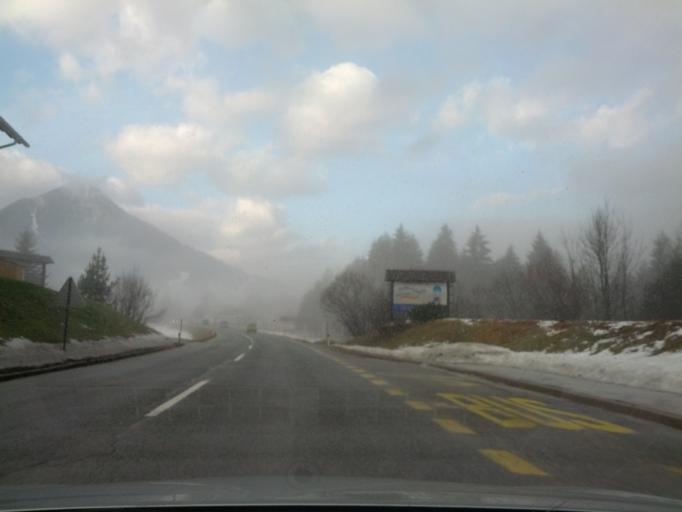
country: SI
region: Kranjska Gora
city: Kranjska Gora
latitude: 46.4878
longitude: 13.8096
